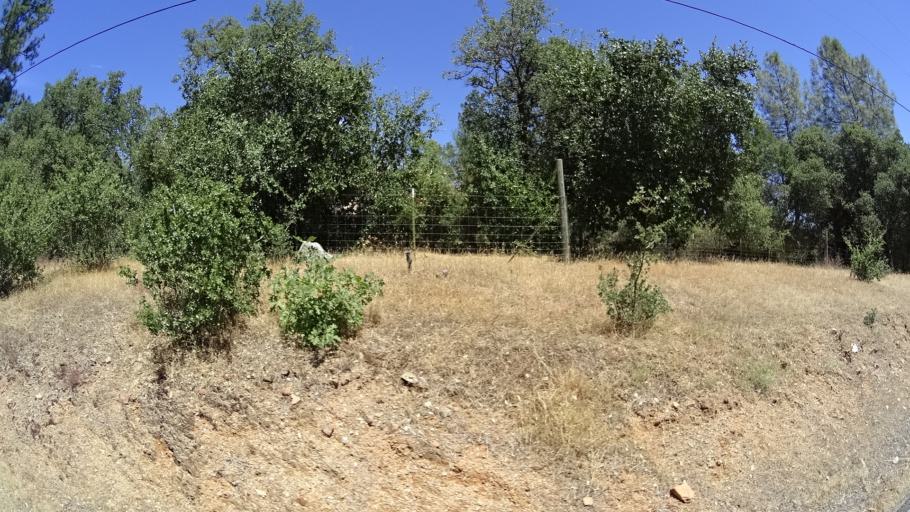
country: US
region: California
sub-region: Calaveras County
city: Mountain Ranch
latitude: 38.2338
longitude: -120.4979
